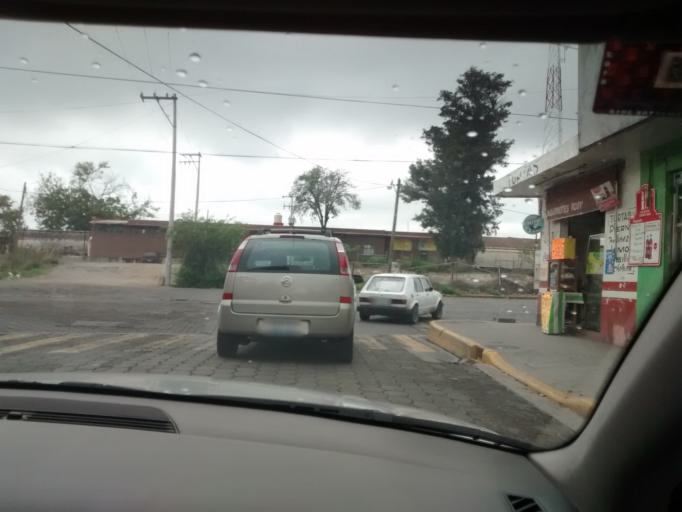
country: MX
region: Puebla
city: Tehuacan
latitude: 18.4612
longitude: -97.4001
